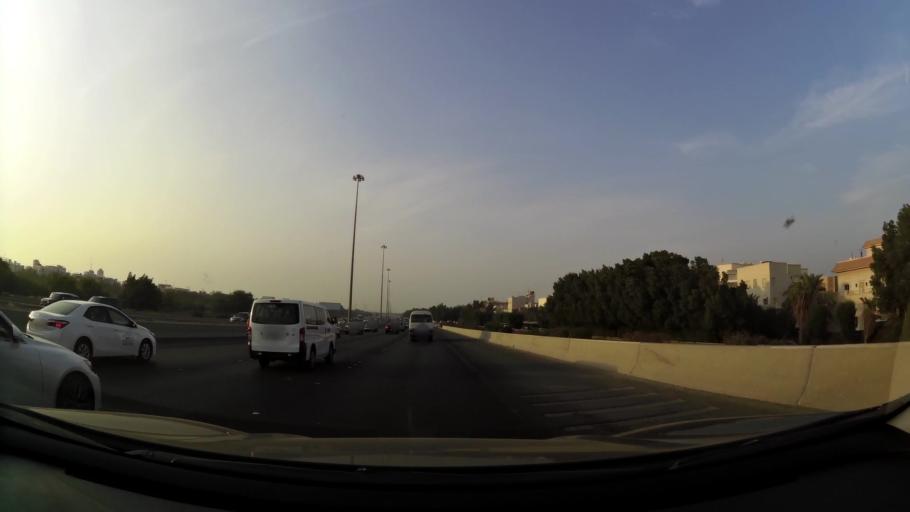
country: KW
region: Muhafazat Hawalli
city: Salwa
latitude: 29.2725
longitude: 48.0830
